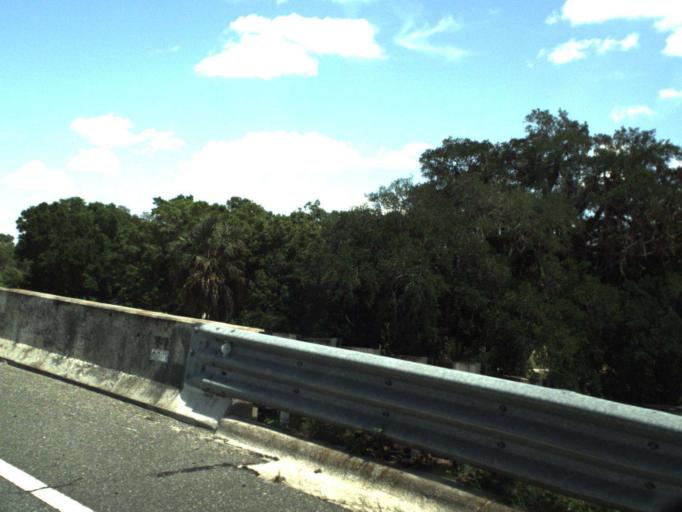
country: US
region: Florida
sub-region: Marion County
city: Ocala
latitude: 29.1974
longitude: -82.1329
